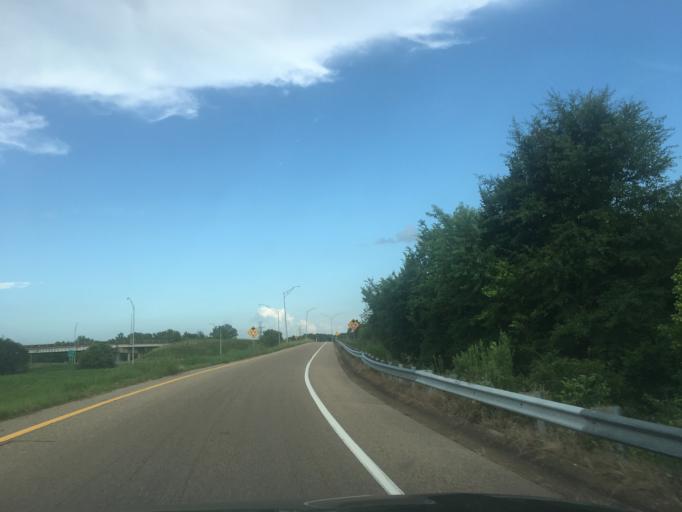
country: US
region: Tennessee
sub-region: Shelby County
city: New South Memphis
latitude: 35.0798
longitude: -90.0598
